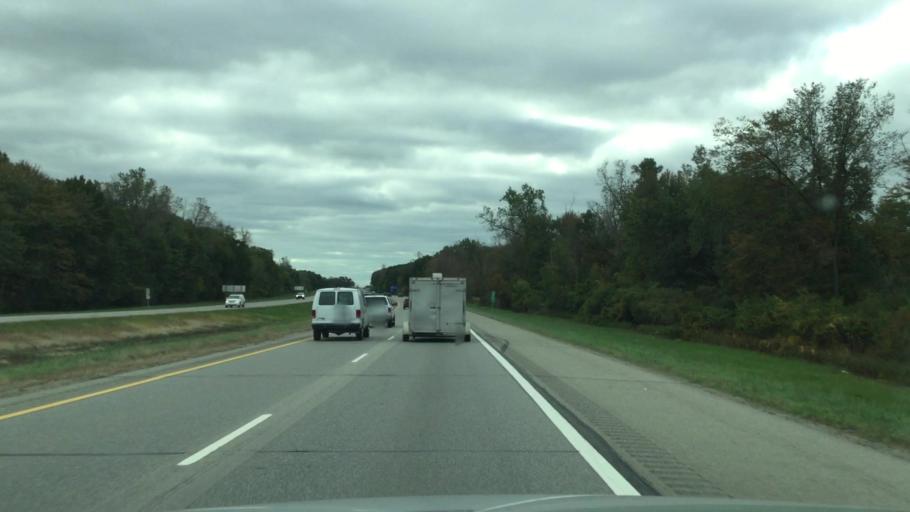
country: US
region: Michigan
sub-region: Macomb County
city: Shelby
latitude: 42.6960
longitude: -83.0235
